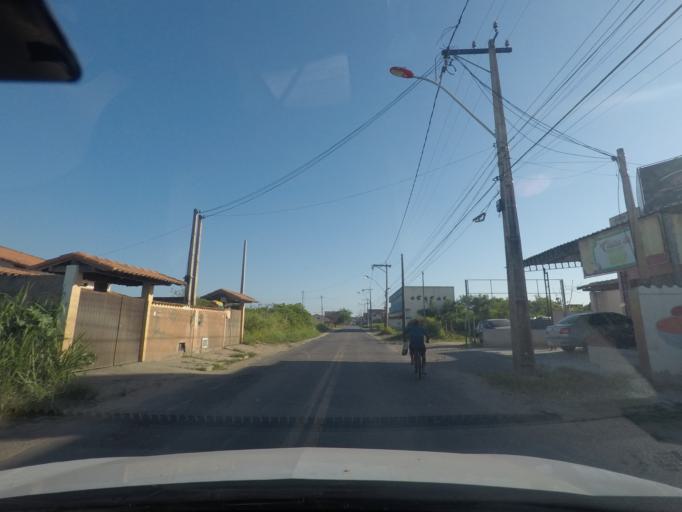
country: BR
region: Rio de Janeiro
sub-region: Marica
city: Marica
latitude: -22.9610
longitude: -42.9424
